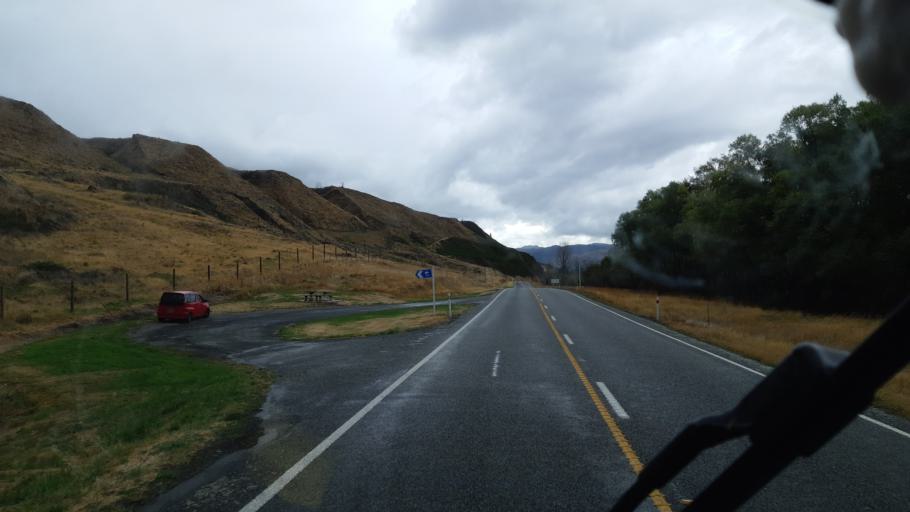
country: NZ
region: Canterbury
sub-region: Hurunui District
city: Amberley
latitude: -42.5786
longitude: 172.7491
